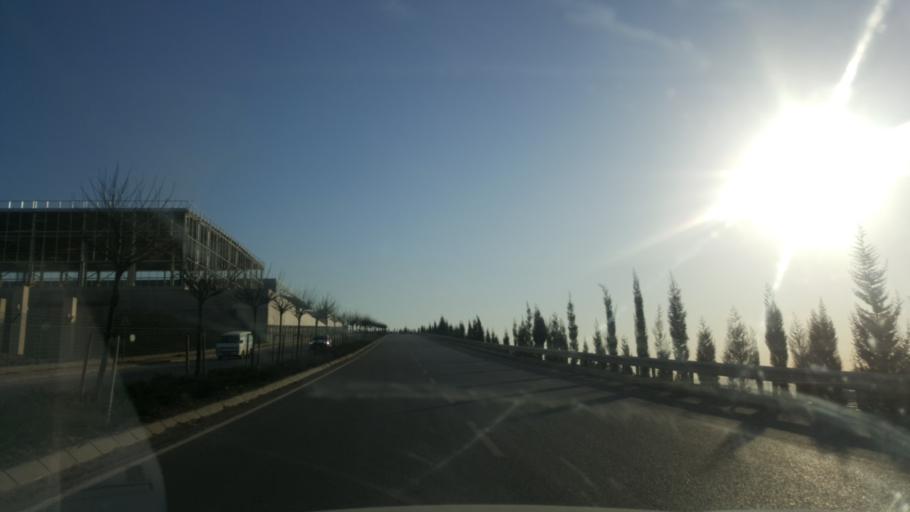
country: TR
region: Kocaeli
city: Tavsanli
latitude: 40.8265
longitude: 29.5609
